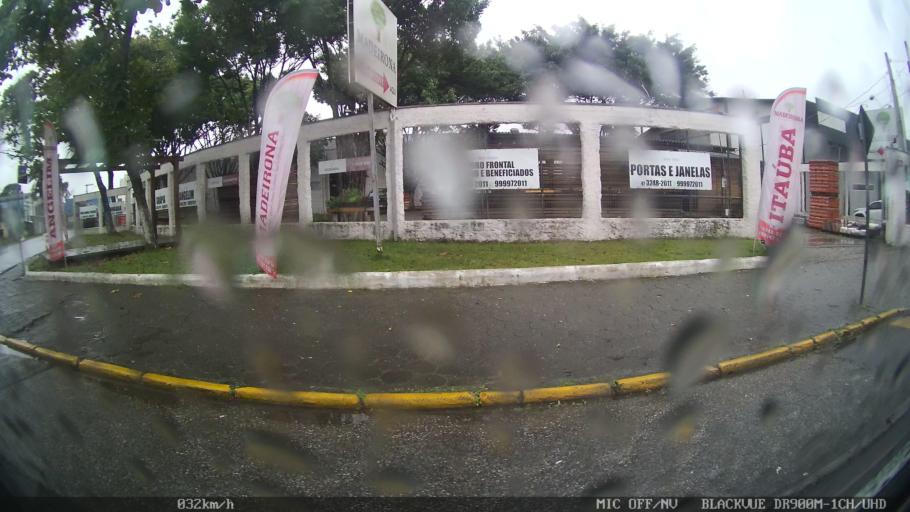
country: BR
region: Santa Catarina
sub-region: Itajai
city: Itajai
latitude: -26.9030
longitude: -48.6777
